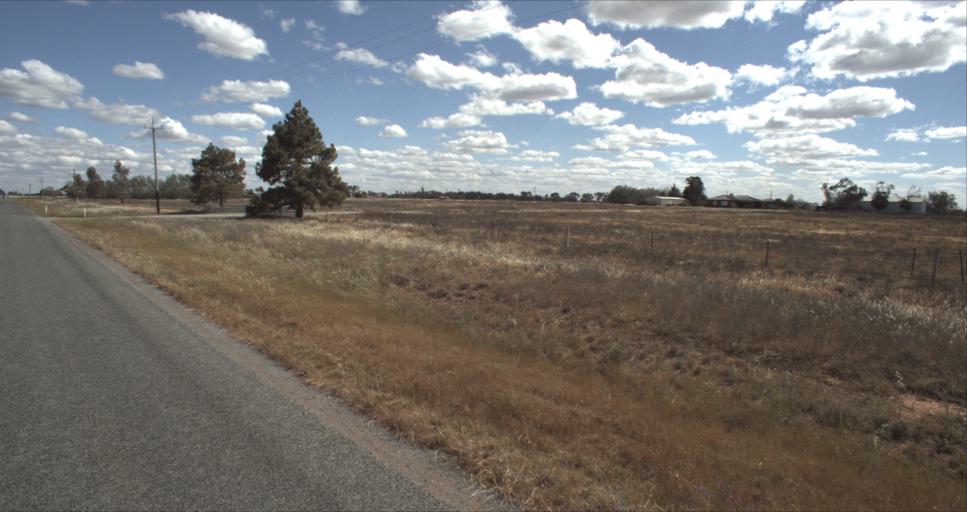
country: AU
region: New South Wales
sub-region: Leeton
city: Leeton
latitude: -34.4565
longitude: 146.2535
